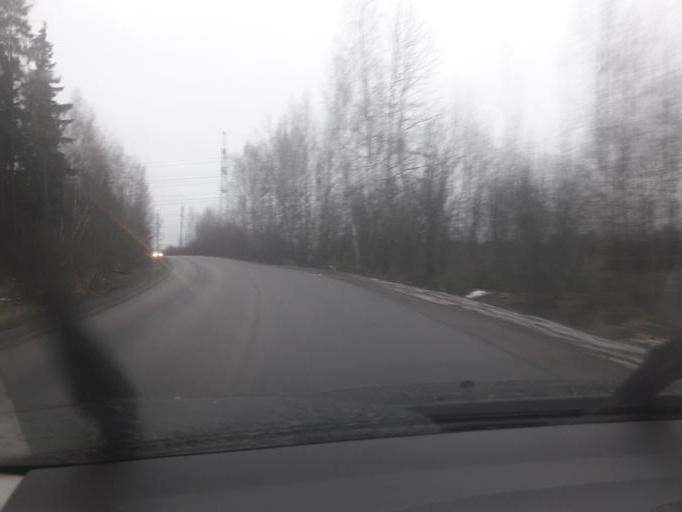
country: RU
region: Moskovskaya
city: Fryazevo
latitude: 55.7569
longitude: 38.5177
